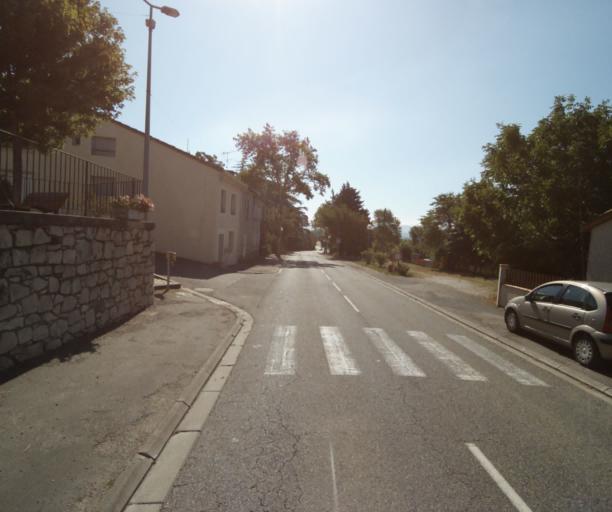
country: FR
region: Midi-Pyrenees
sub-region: Departement de la Haute-Garonne
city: Saint-Felix-Lauragais
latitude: 43.4784
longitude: 1.9239
